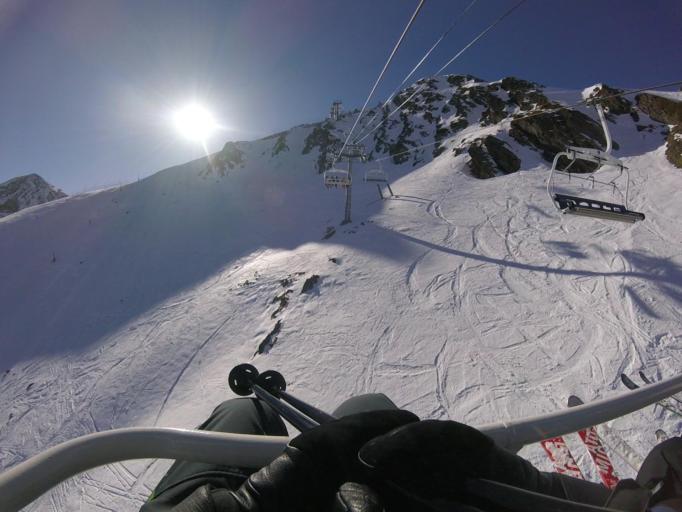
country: AD
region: Encamp
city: Pas de la Casa
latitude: 42.5288
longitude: 1.7257
